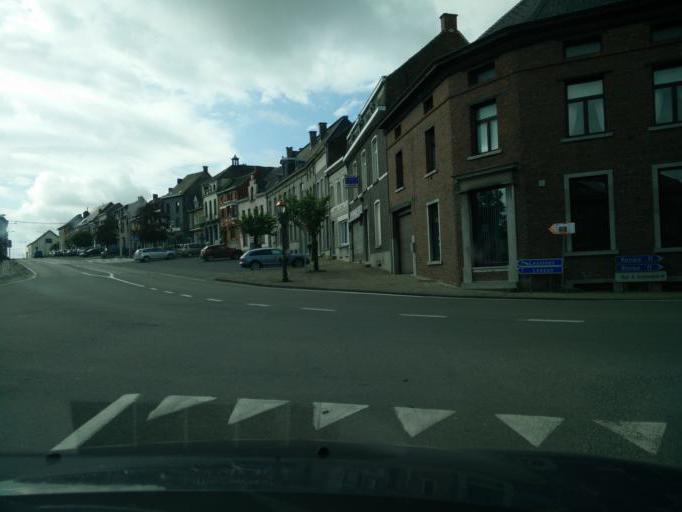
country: BE
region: Wallonia
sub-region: Province du Hainaut
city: Flobecq
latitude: 50.7373
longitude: 3.7375
